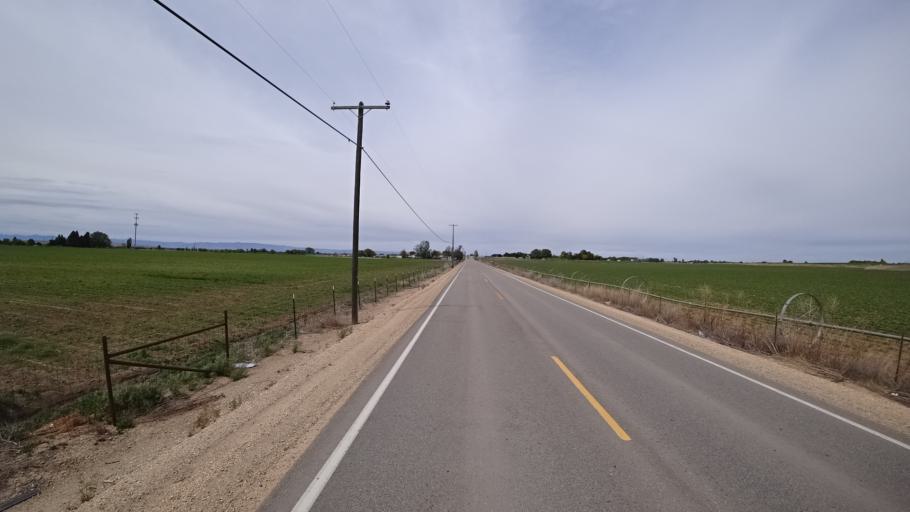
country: US
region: Idaho
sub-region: Ada County
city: Kuna
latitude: 43.5319
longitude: -116.3579
